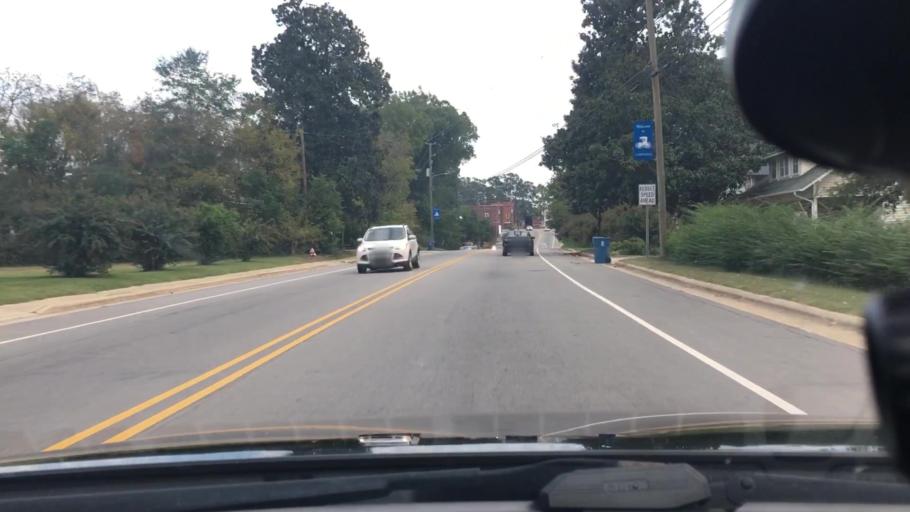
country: US
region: North Carolina
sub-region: Moore County
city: Carthage
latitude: 35.3489
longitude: -79.4198
